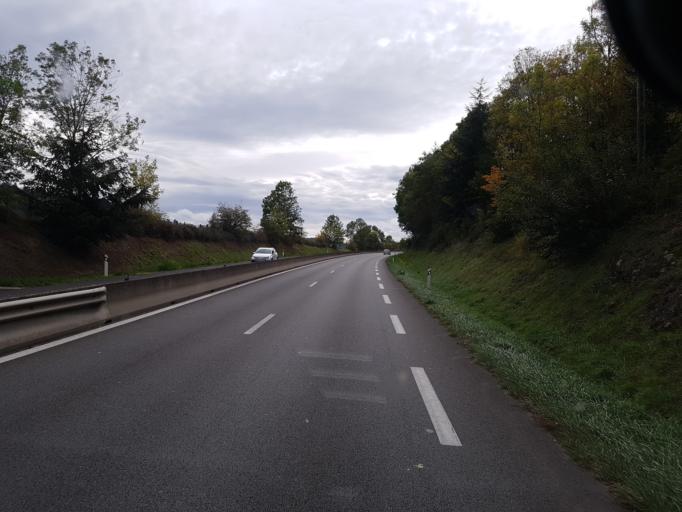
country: FR
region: Rhone-Alpes
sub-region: Departement de la Loire
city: Saint-Genest-Lerpt
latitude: 45.4599
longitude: 4.3372
